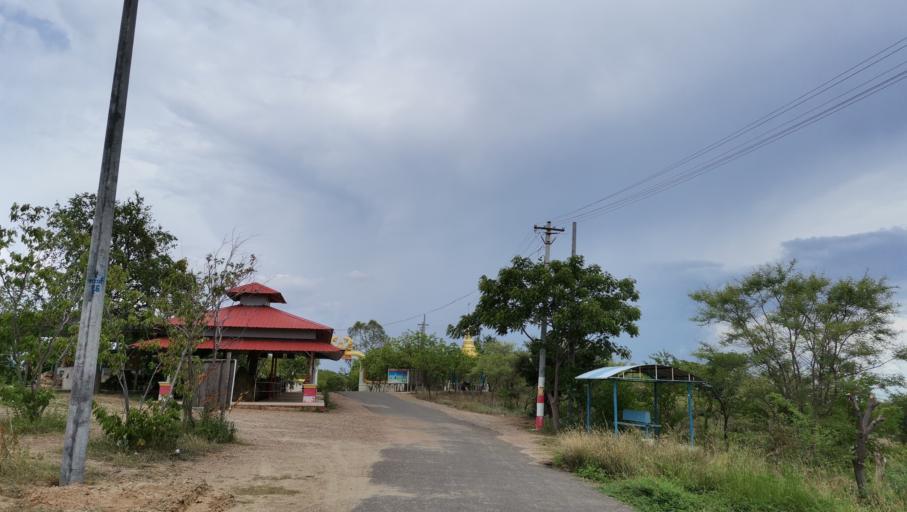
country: MM
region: Mandalay
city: Myingyan
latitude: 21.8253
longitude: 95.3937
